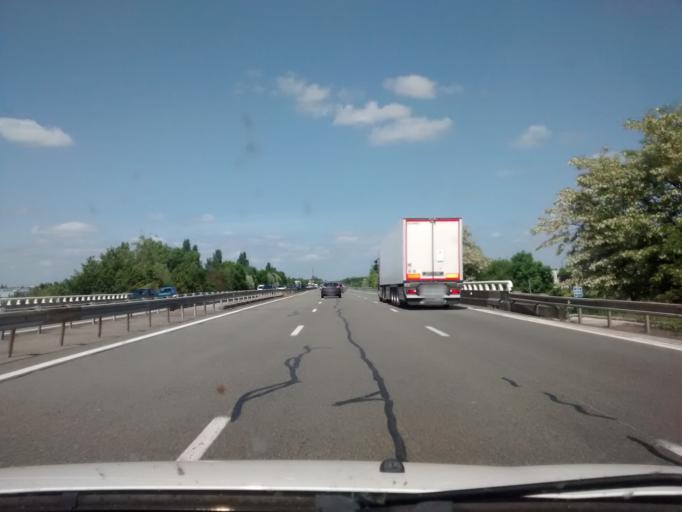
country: FR
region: Centre
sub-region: Departement d'Eure-et-Loir
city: Le Coudray
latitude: 48.4266
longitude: 1.5154
